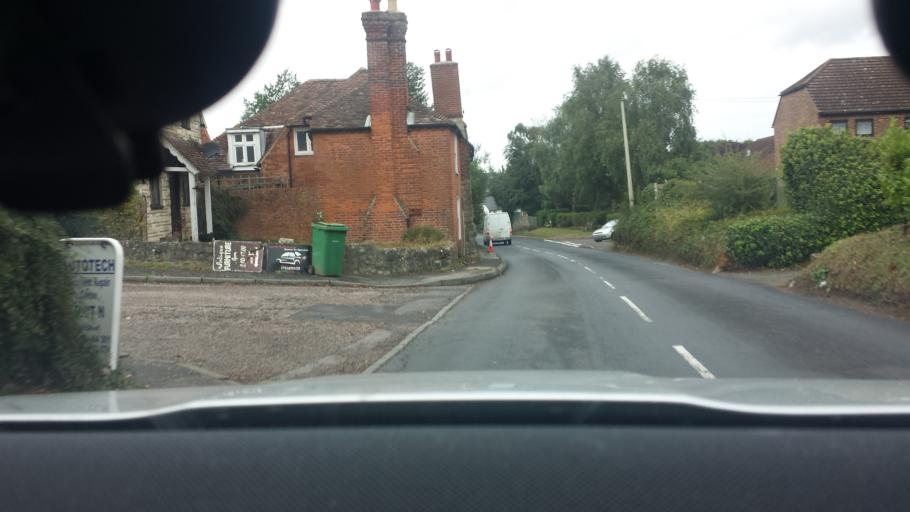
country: GB
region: England
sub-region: Kent
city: Harrietsham
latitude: 51.2448
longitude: 0.6059
